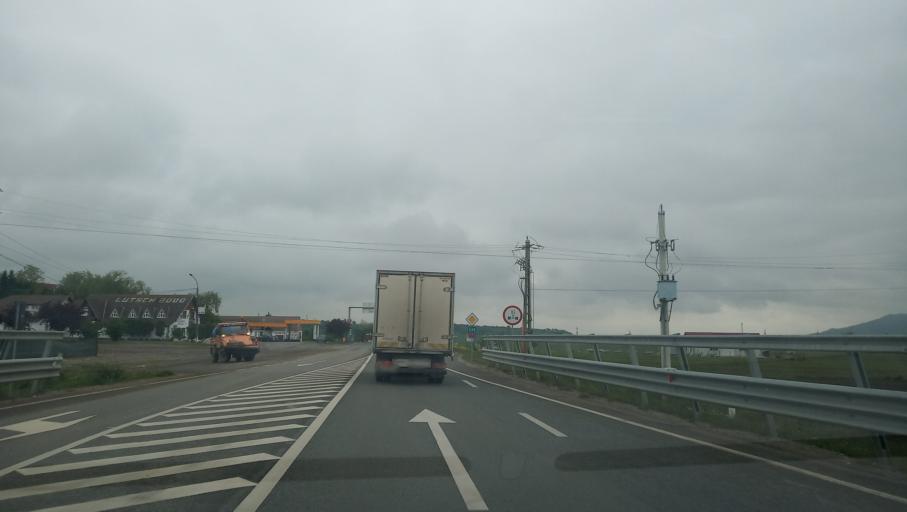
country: RO
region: Alba
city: Vurpar
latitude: 45.9742
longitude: 23.4627
